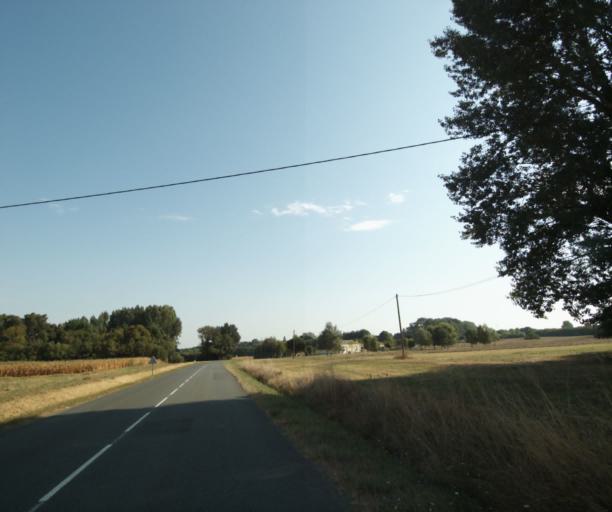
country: FR
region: Poitou-Charentes
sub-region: Departement de la Charente-Maritime
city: Tonnay-Charente
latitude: 45.9579
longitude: -0.8889
